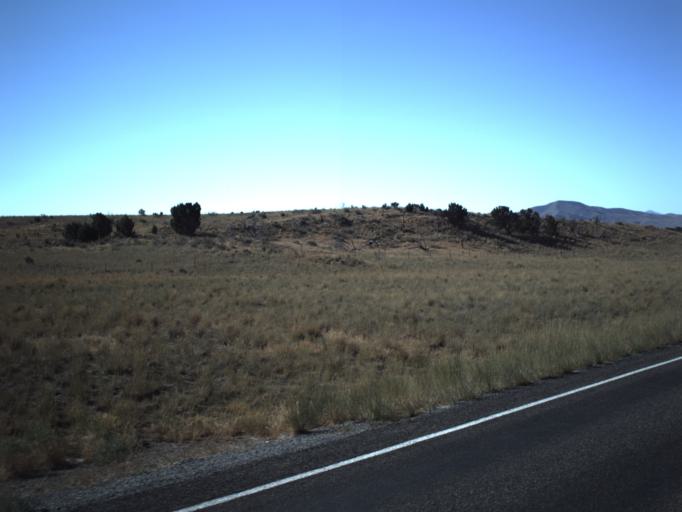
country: US
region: Utah
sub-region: Juab County
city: Mona
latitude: 39.7457
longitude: -112.1862
